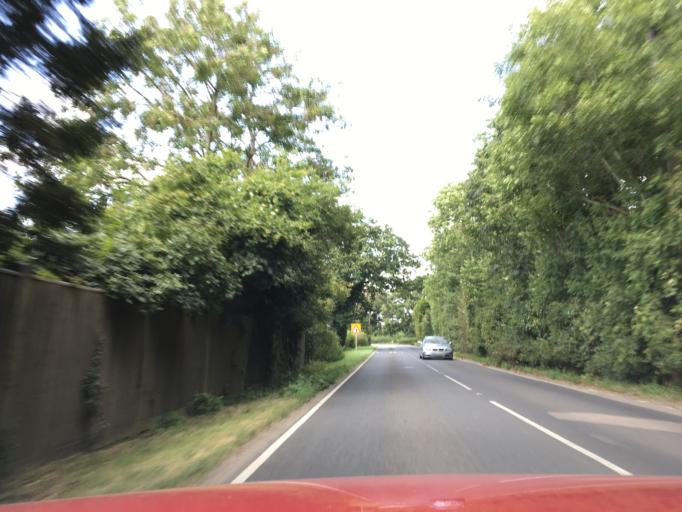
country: GB
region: England
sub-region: Kent
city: Tenterden
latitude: 51.1094
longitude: 0.6454
